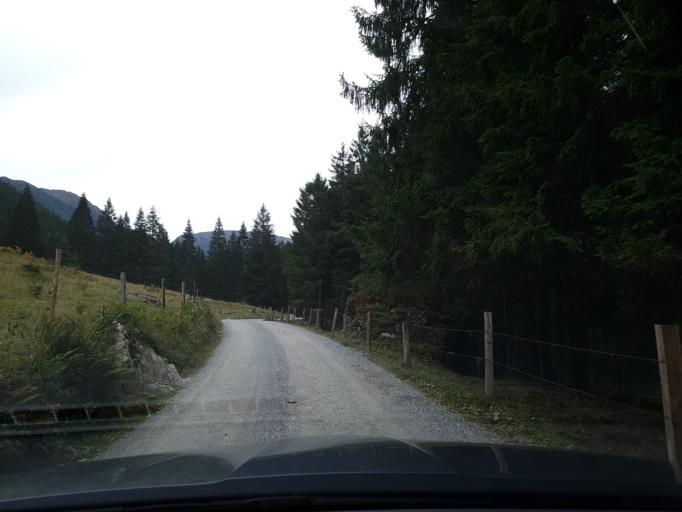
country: AT
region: Salzburg
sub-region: Politischer Bezirk Sankt Johann im Pongau
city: Forstau
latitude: 47.3297
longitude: 13.5768
